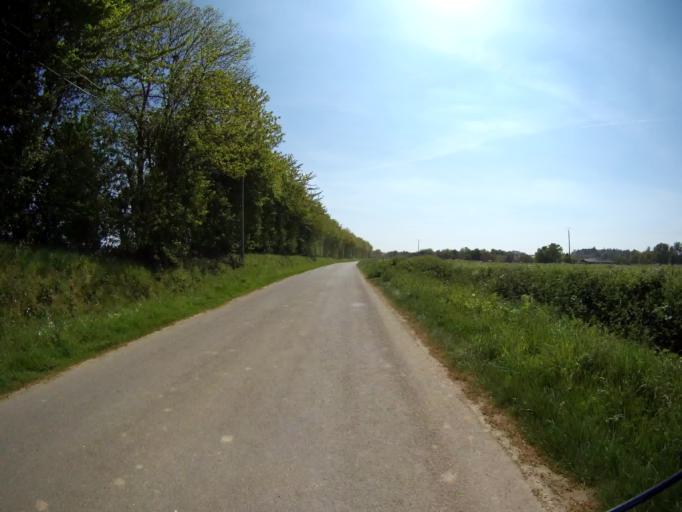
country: FR
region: Brittany
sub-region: Departement d'Ille-et-Vilaine
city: Vern-sur-Seiche
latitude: 48.0300
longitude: -1.6239
